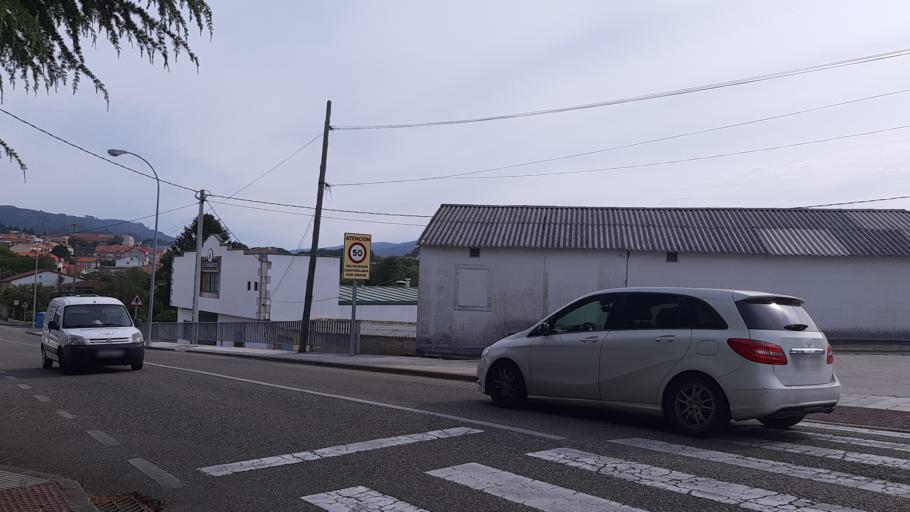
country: ES
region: Galicia
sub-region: Provincia de Pontevedra
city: O Rosal
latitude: 41.9301
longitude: -8.8371
